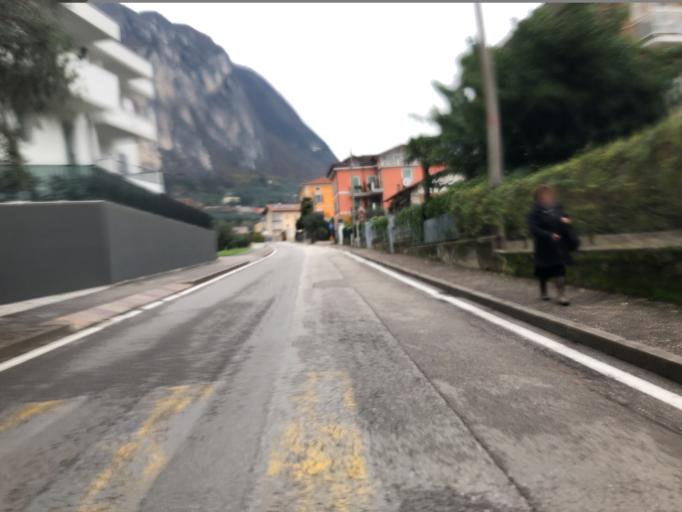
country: IT
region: Trentino-Alto Adige
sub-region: Provincia di Trento
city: Riva del Garda
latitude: 45.8916
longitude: 10.8383
